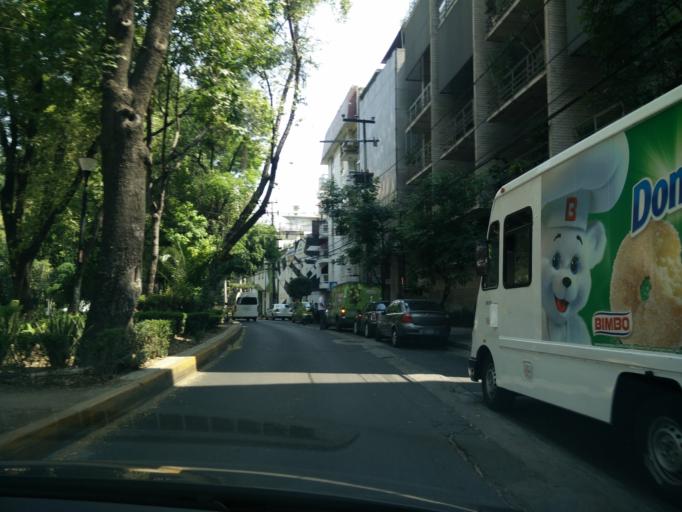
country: MX
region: Mexico City
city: Benito Juarez
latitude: 19.4144
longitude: -99.1667
